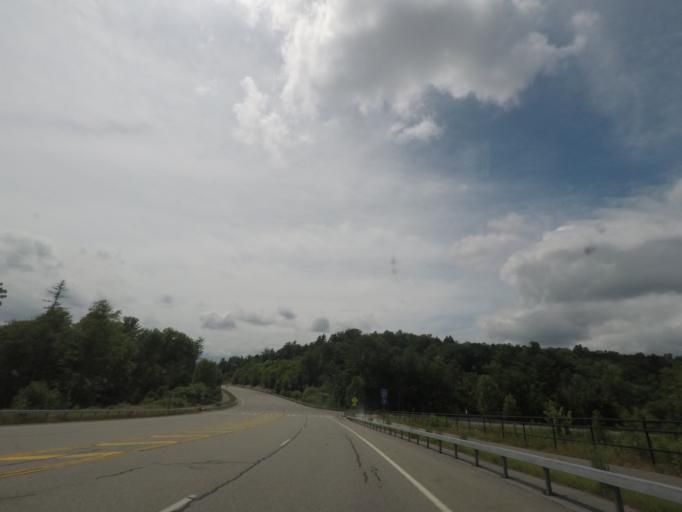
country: US
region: New York
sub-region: Saratoga County
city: Country Knolls
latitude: 42.9548
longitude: -73.7751
